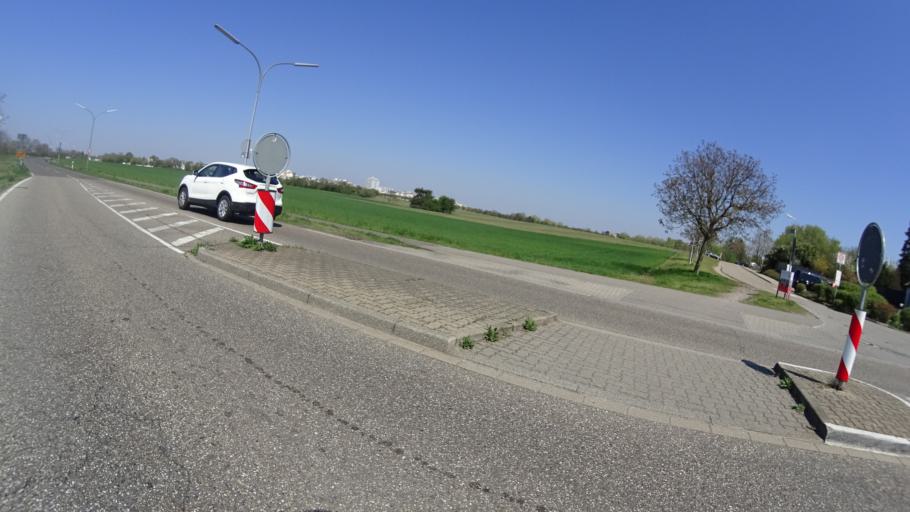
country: DE
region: Baden-Wuerttemberg
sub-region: Karlsruhe Region
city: Karlsruhe
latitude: 49.0374
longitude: 8.3825
